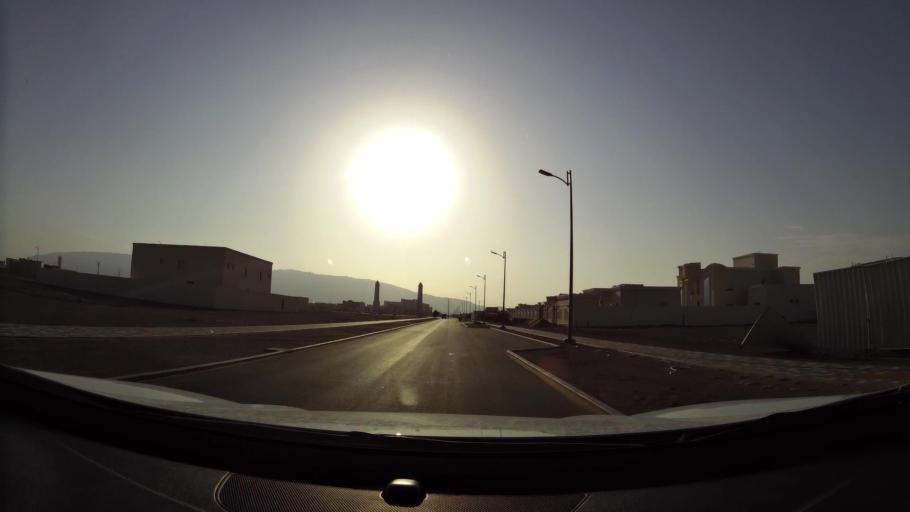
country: AE
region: Abu Dhabi
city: Al Ain
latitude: 24.1118
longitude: 55.8532
